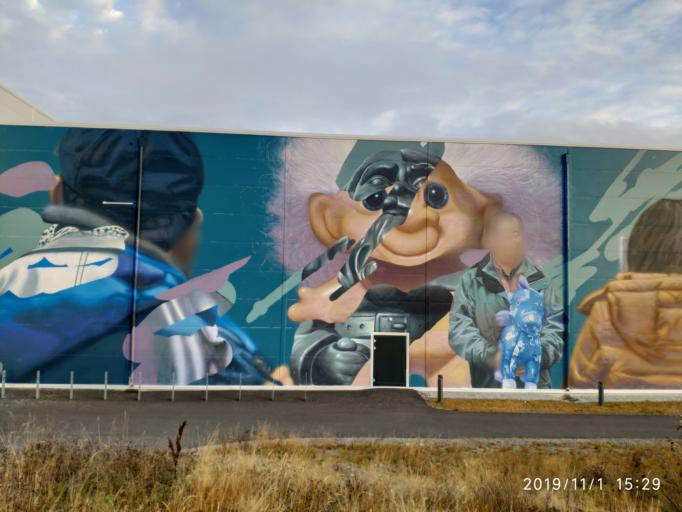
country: NO
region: Buskerud
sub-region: Gol
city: Gol
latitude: 60.7049
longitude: 8.9397
